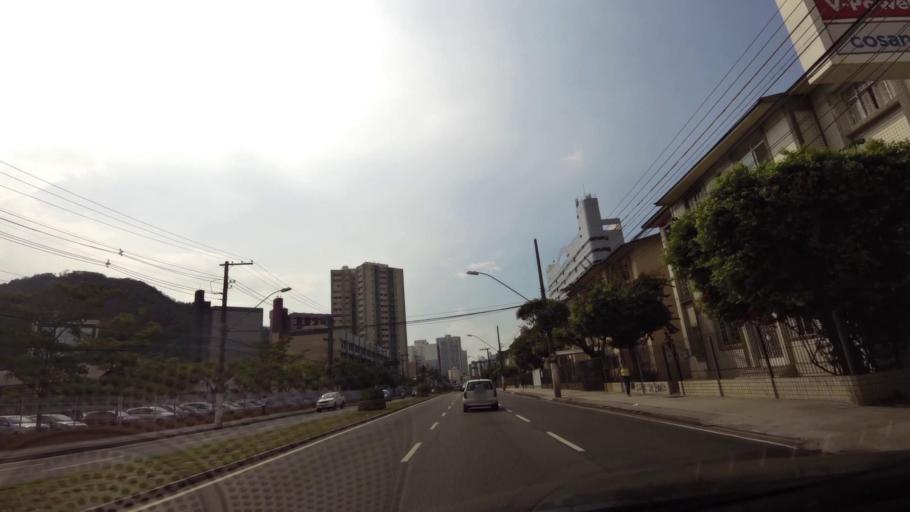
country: BR
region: Espirito Santo
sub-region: Vila Velha
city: Vila Velha
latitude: -20.3115
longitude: -40.3025
